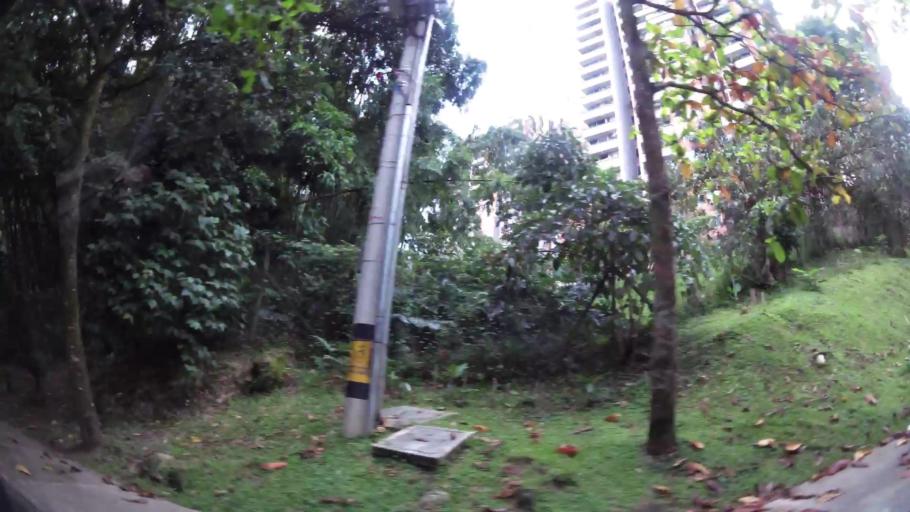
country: CO
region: Antioquia
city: Envigado
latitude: 6.1582
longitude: -75.5973
